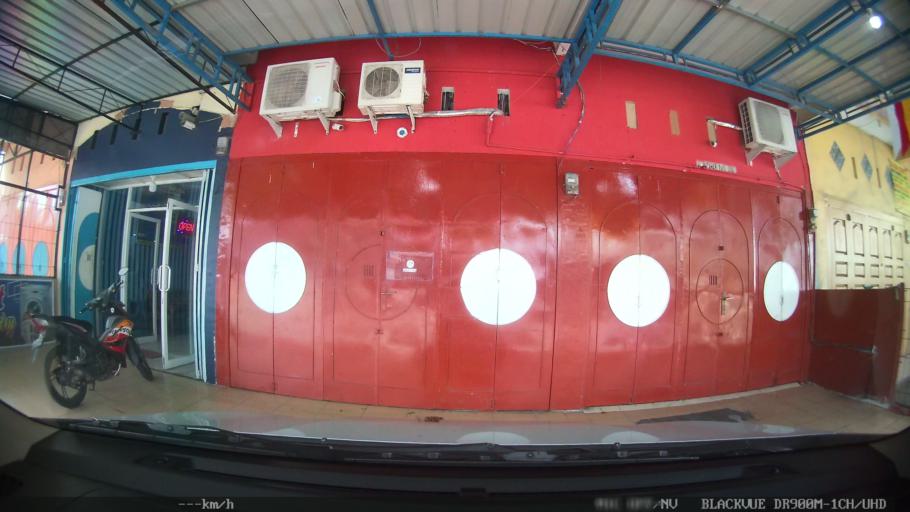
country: ID
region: North Sumatra
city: Sunggal
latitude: 3.6098
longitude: 98.6306
